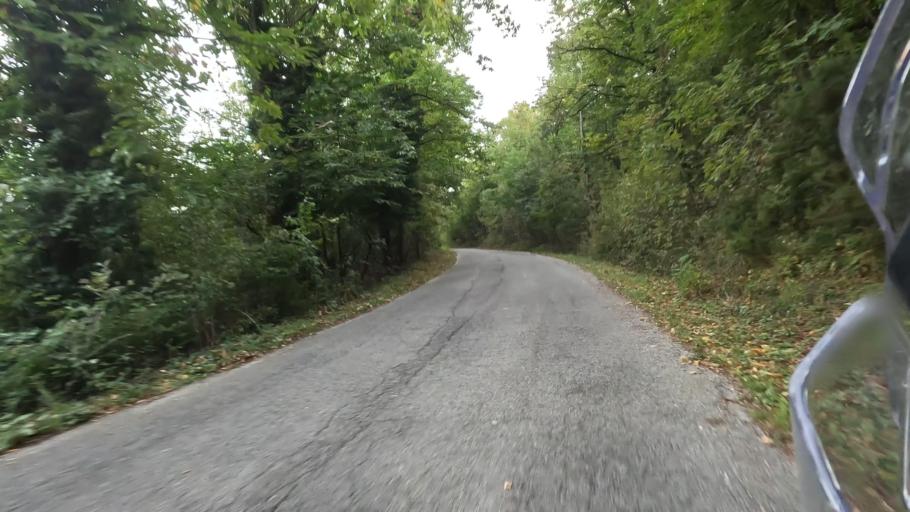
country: IT
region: Liguria
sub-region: Provincia di Savona
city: San Giovanni
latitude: 44.3943
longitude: 8.5362
